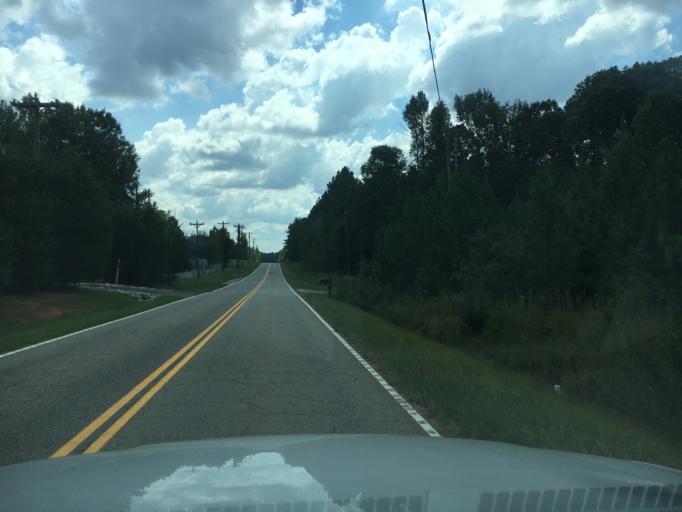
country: US
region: South Carolina
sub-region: Greenwood County
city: Greenwood
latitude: 34.1277
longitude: -82.1264
